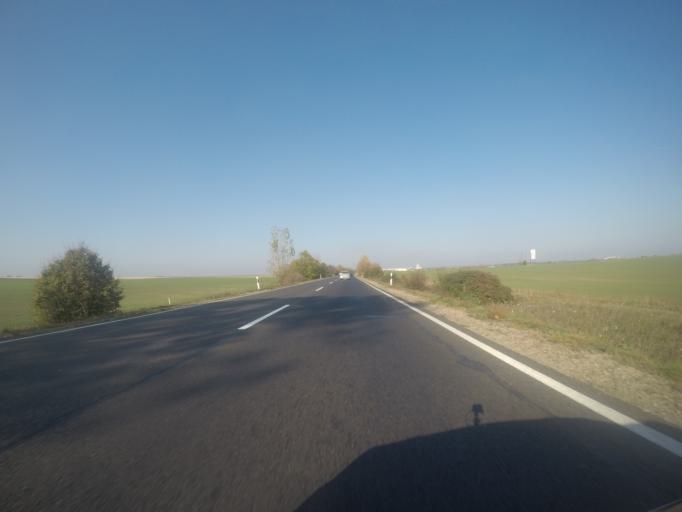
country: HU
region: Fejer
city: Baracs
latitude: 46.8864
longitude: 18.9194
